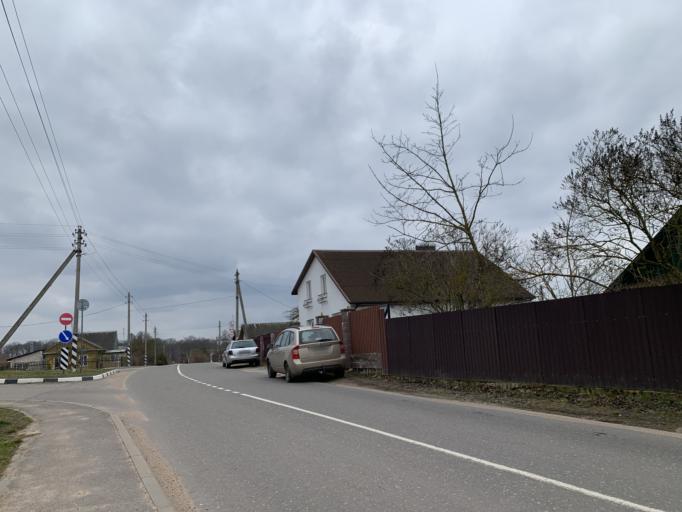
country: BY
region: Minsk
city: Nyasvizh
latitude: 53.2322
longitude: 26.6883
